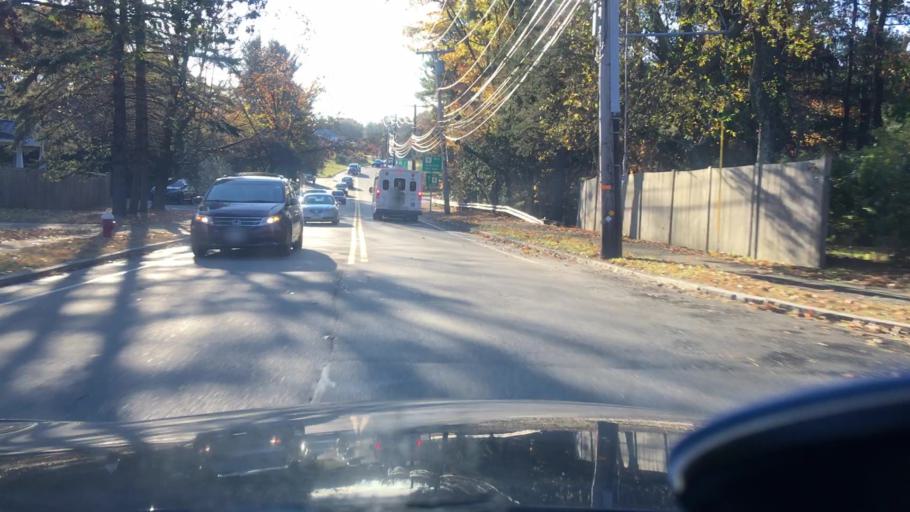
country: US
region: Massachusetts
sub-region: Norfolk County
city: Needham
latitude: 42.3183
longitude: -71.2484
